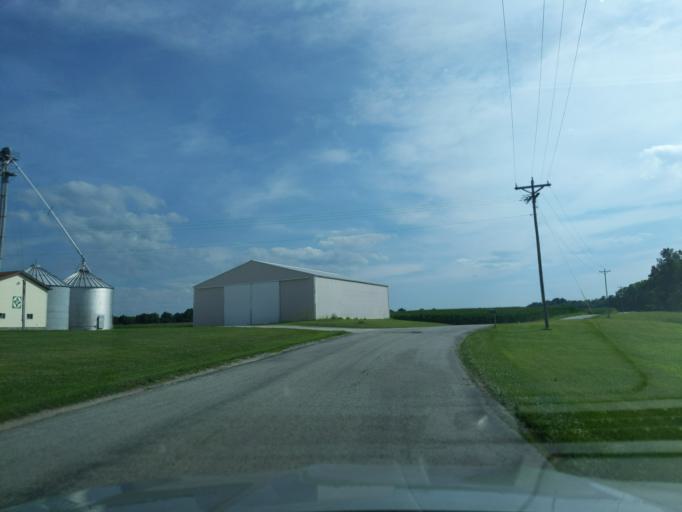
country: US
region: Indiana
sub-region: Decatur County
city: Greensburg
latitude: 39.2597
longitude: -85.4662
